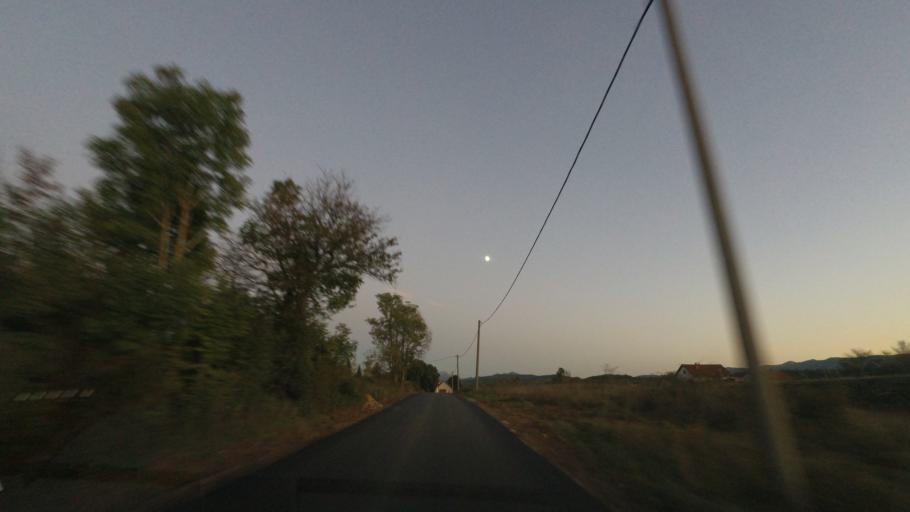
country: HR
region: Zadarska
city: Obrovac
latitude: 44.3749
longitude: 15.6662
